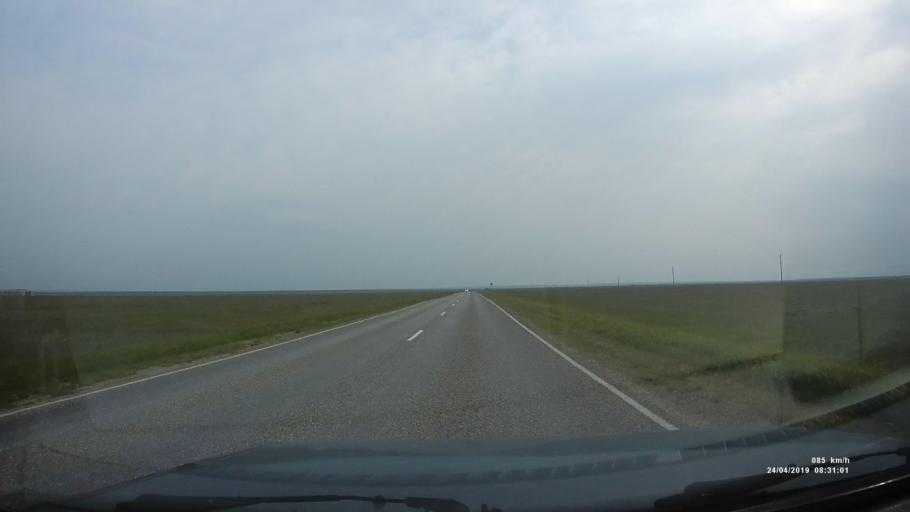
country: RU
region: Kalmykiya
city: Priyutnoye
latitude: 46.1639
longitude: 43.8541
